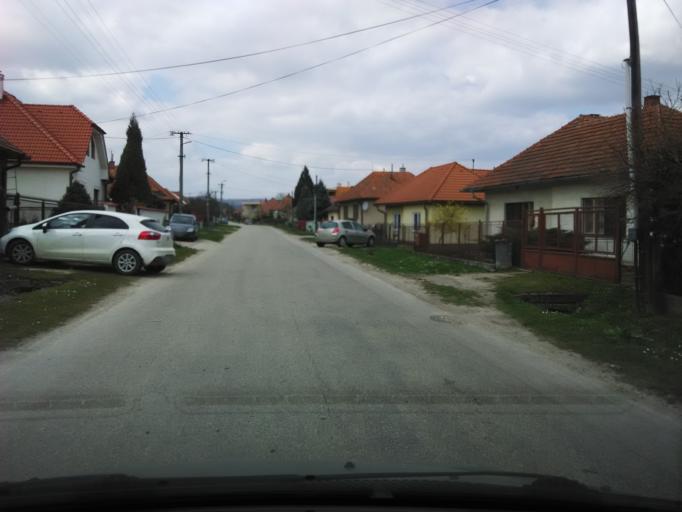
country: SK
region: Nitriansky
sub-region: Okres Nitra
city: Nitra
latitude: 48.3812
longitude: 18.2201
